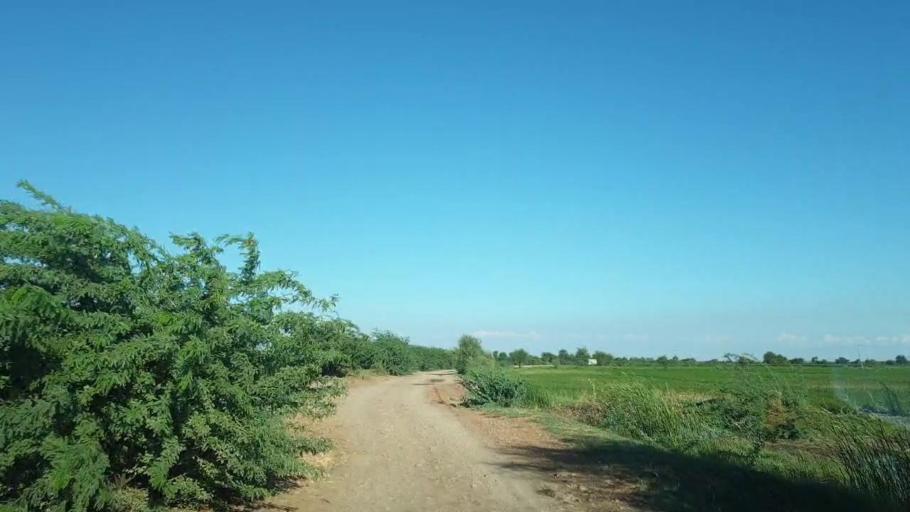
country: PK
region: Sindh
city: Dhoro Naro
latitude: 25.6382
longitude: 69.5059
